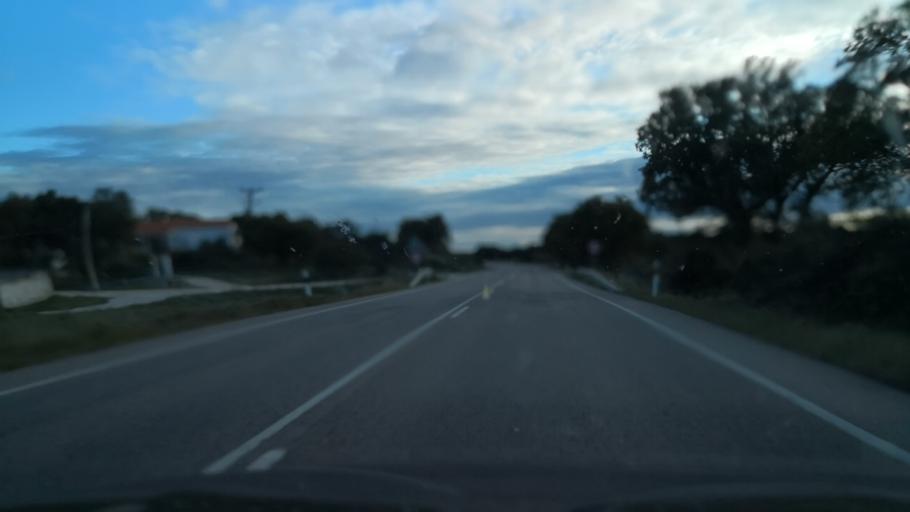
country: ES
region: Extremadura
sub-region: Provincia de Caceres
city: Caceres
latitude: 39.3974
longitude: -6.4238
